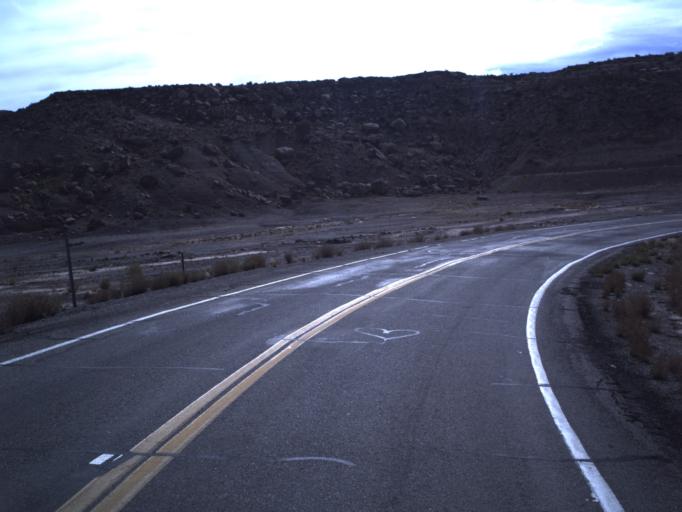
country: US
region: Utah
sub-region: San Juan County
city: Blanding
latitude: 37.3282
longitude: -109.3185
